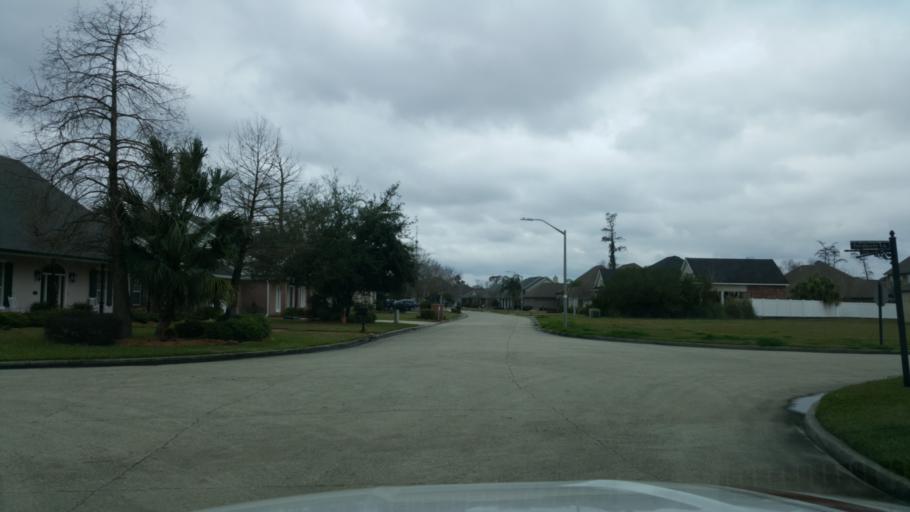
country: US
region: Louisiana
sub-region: Jefferson Parish
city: Woodmere
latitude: 29.8753
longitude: -90.0771
